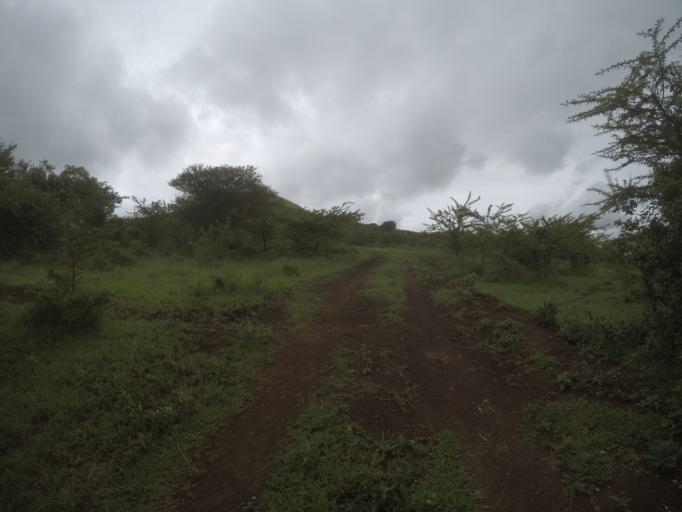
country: ZA
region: KwaZulu-Natal
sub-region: uThungulu District Municipality
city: Empangeni
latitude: -28.6030
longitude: 31.8532
